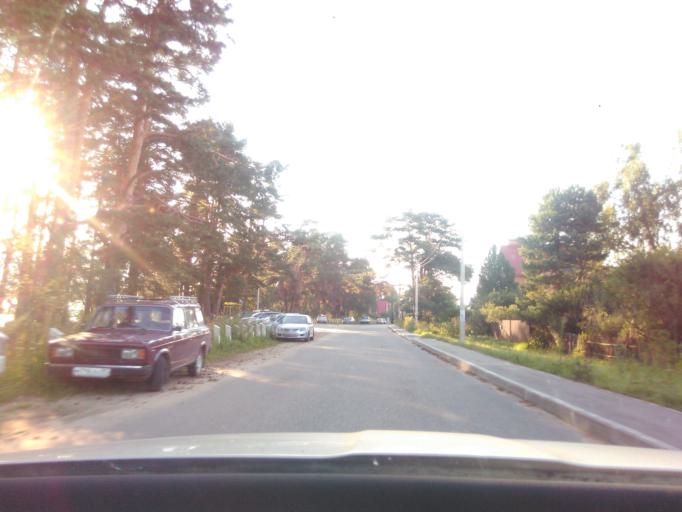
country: RU
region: Tverskaya
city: Konakovo
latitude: 56.7519
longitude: 36.7567
